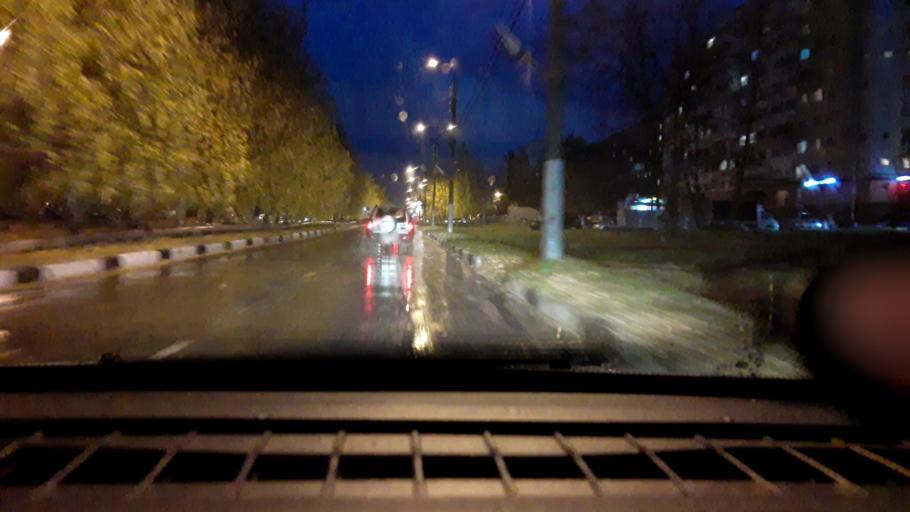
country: RU
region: Nizjnij Novgorod
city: Kstovo
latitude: 56.1584
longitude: 44.2091
